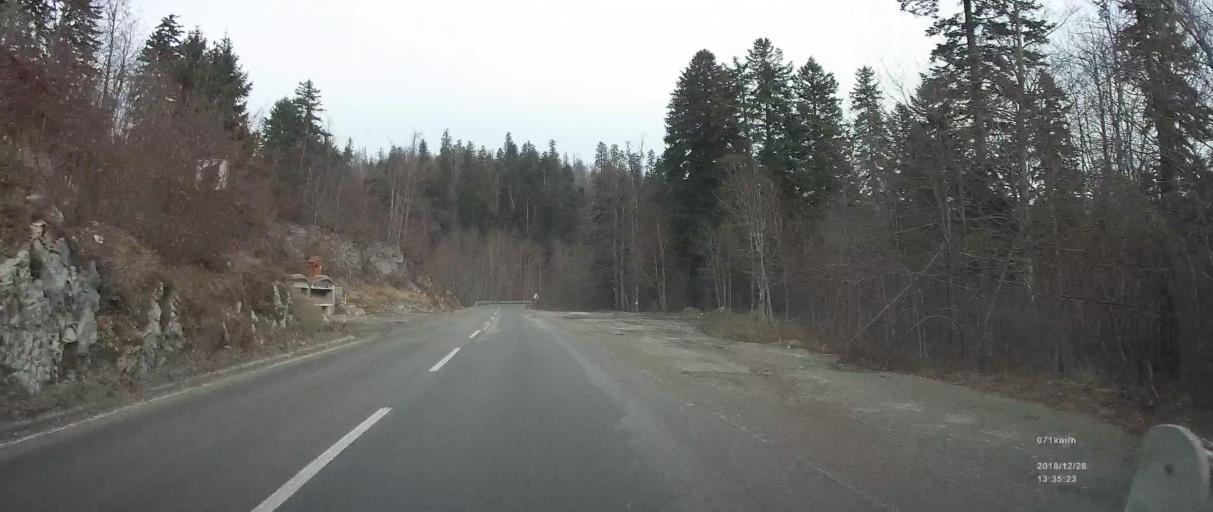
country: HR
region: Primorsko-Goranska
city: Hreljin
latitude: 45.3491
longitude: 14.6915
